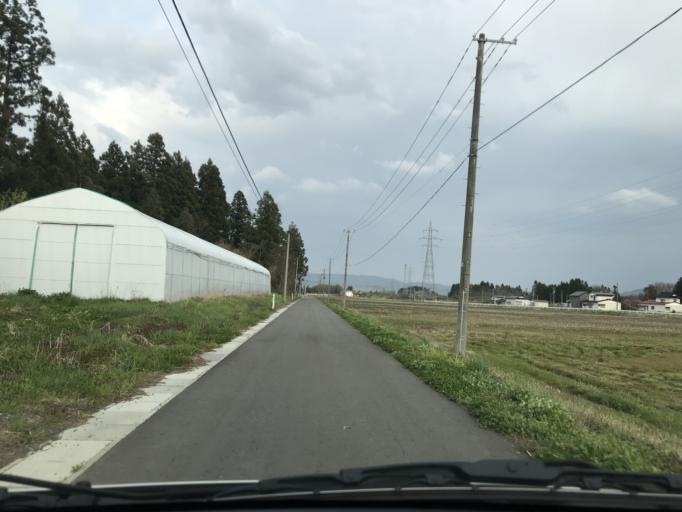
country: JP
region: Iwate
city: Mizusawa
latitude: 39.0984
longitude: 141.1059
